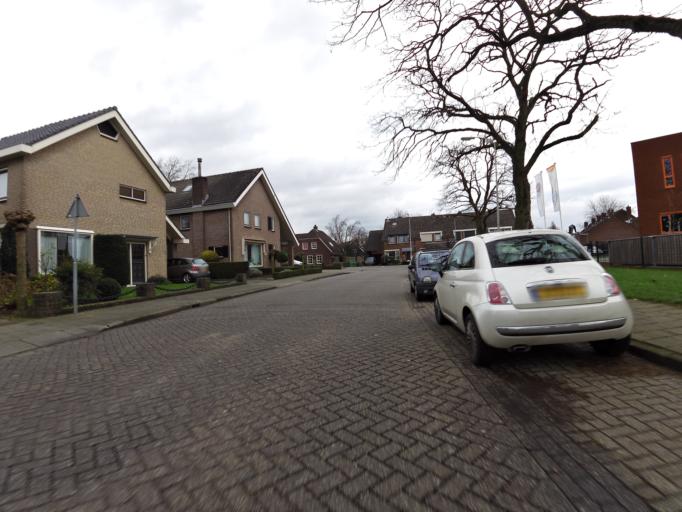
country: NL
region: Gelderland
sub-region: Gemeente Zevenaar
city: Zevenaar
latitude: 51.9456
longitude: 6.1321
